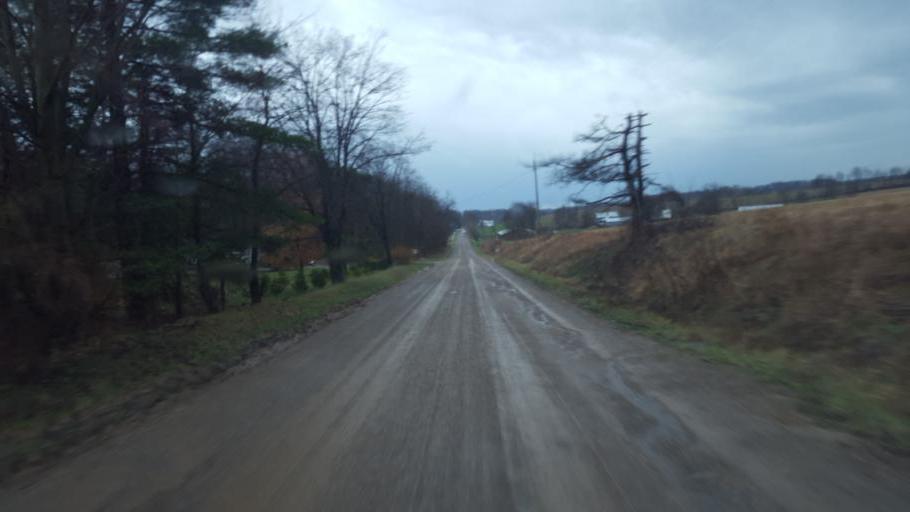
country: US
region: Ohio
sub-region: Knox County
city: Danville
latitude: 40.5435
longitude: -82.3600
